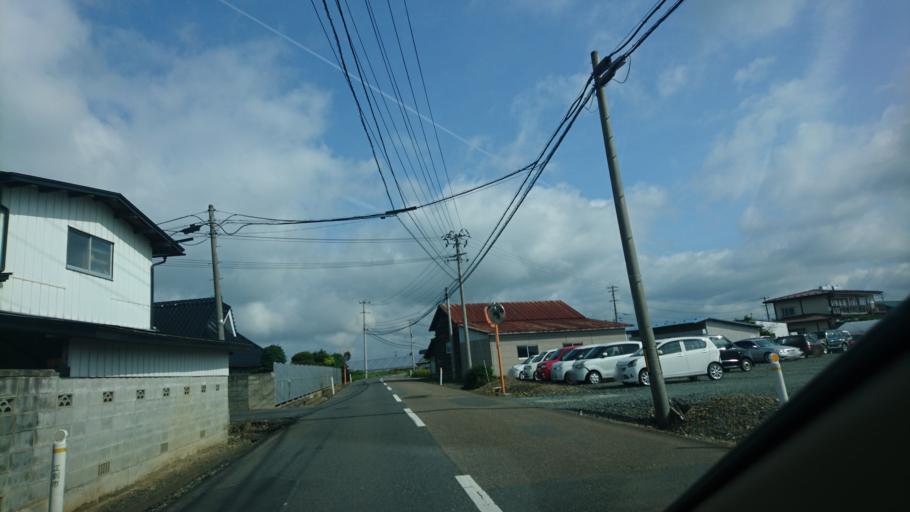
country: JP
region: Iwate
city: Mizusawa
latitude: 39.1596
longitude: 141.1780
